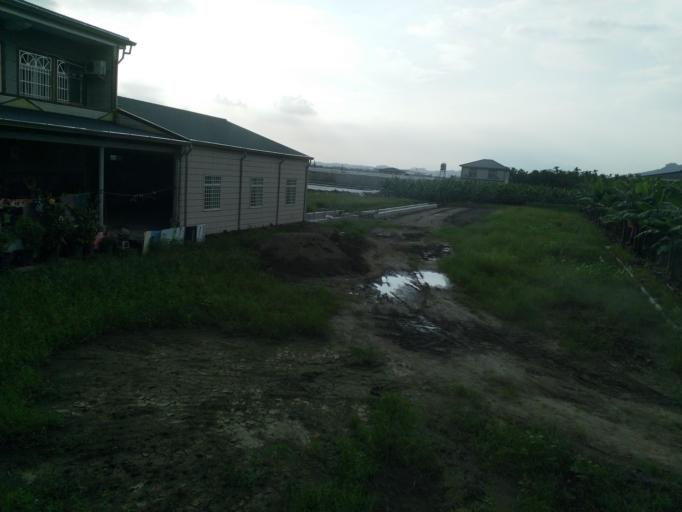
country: TW
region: Taiwan
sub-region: Pingtung
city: Pingtung
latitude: 22.8743
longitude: 120.5362
